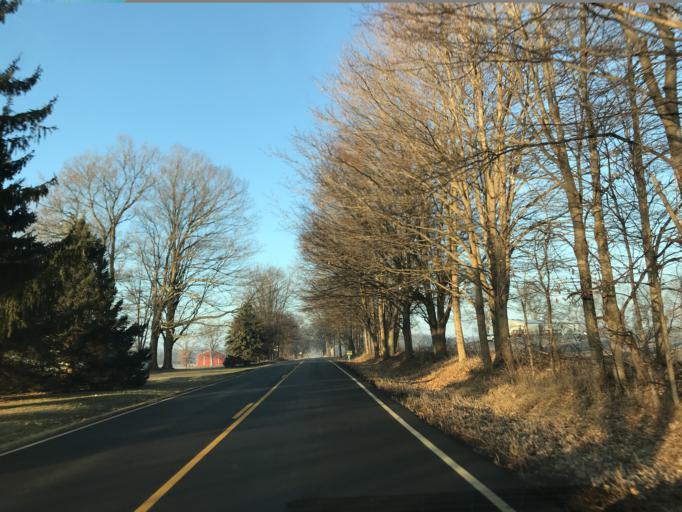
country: US
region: Michigan
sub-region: Ingham County
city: Leslie
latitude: 42.4221
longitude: -84.5236
